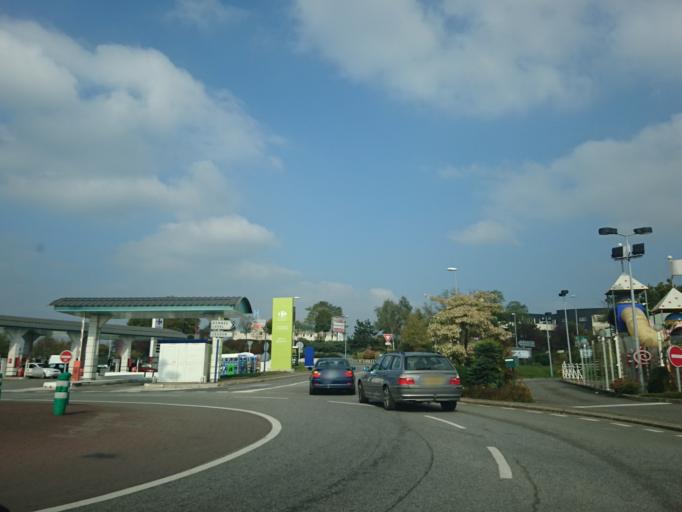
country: FR
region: Brittany
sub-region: Departement d'Ille-et-Vilaine
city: Cesson-Sevigne
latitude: 48.1121
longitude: -1.5892
